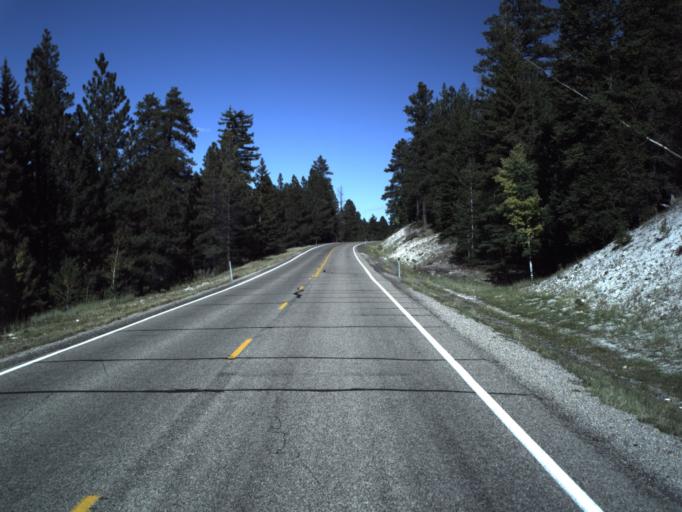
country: US
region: Utah
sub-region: Iron County
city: Parowan
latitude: 37.6991
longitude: -112.6605
